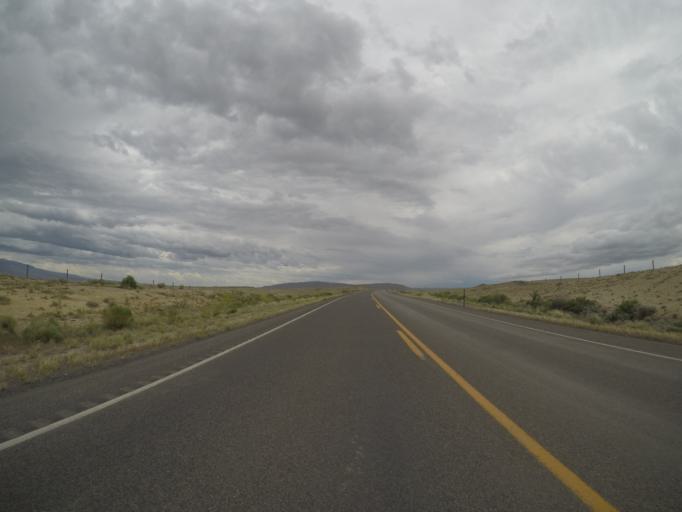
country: US
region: Wyoming
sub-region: Big Horn County
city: Lovell
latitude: 44.8918
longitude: -108.2886
